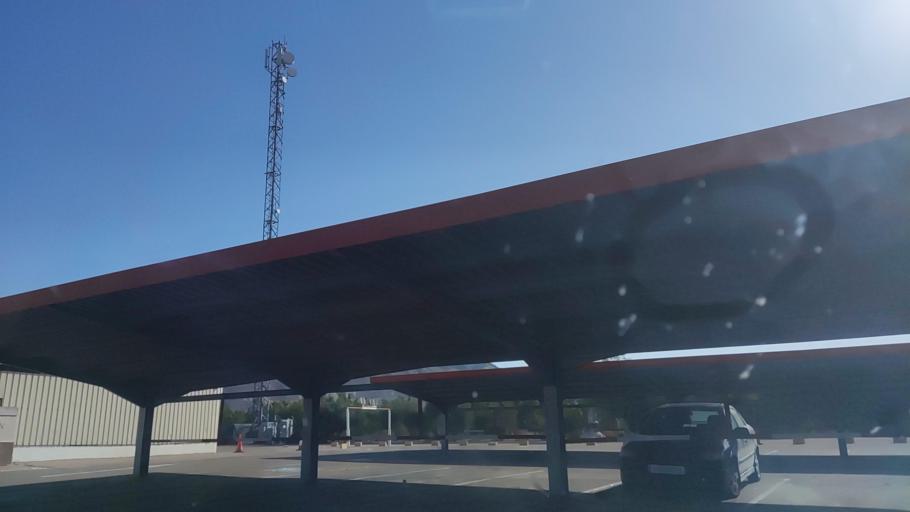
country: ES
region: Castille-La Mancha
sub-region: Provincia de Albacete
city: Hellin
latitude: 38.4652
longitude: -1.5953
